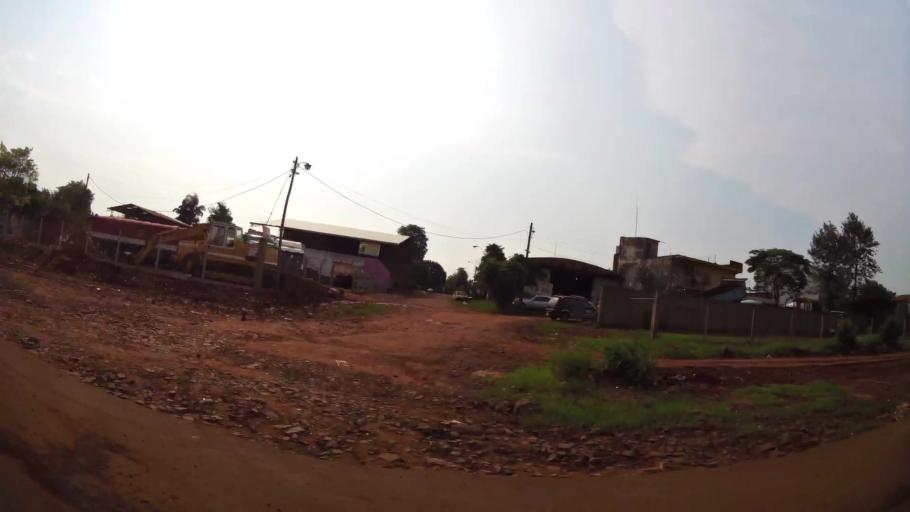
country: PY
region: Alto Parana
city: Ciudad del Este
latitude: -25.4870
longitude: -54.6621
